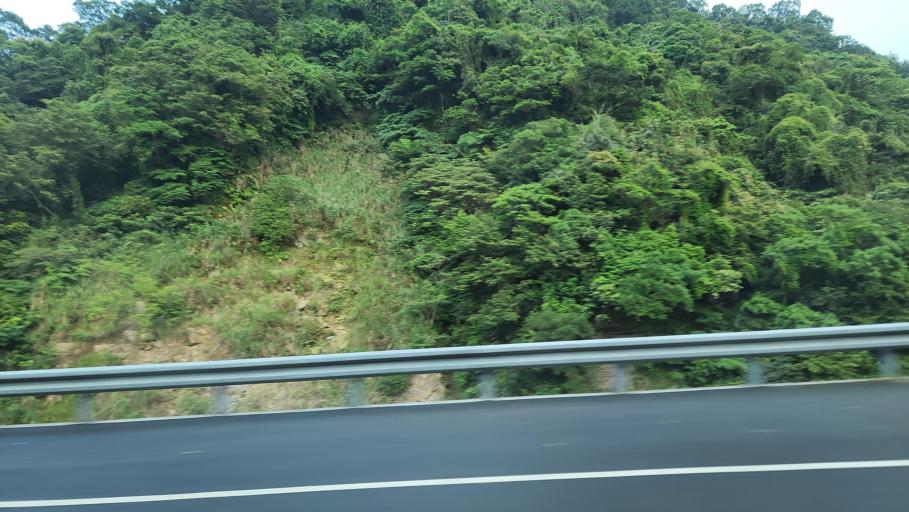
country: TW
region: Taiwan
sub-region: Keelung
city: Keelung
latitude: 25.1633
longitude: 121.6534
